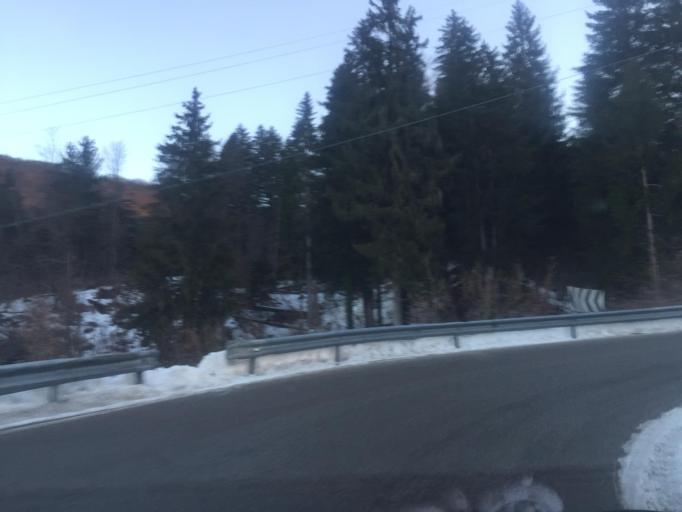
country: IT
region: Friuli Venezia Giulia
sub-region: Provincia di Udine
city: Lauco
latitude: 46.4276
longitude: 12.9229
